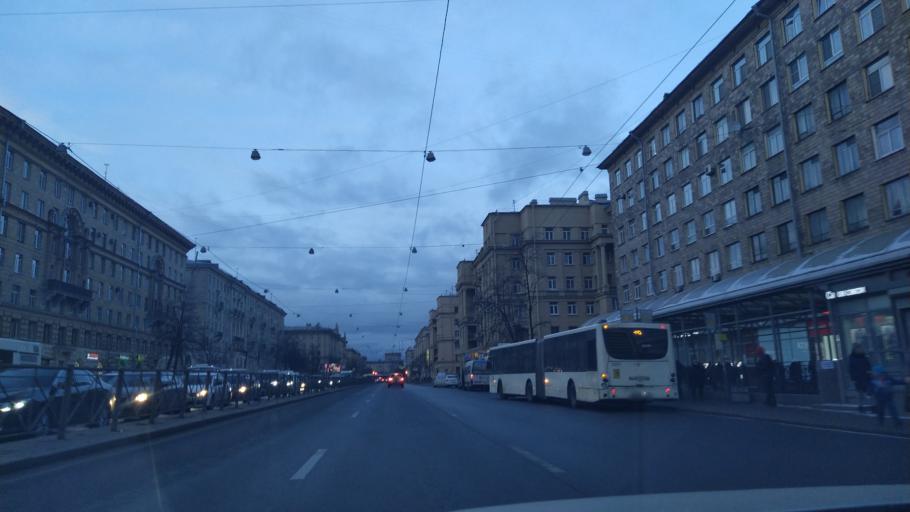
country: RU
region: St.-Petersburg
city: Avtovo
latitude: 59.8677
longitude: 30.2606
